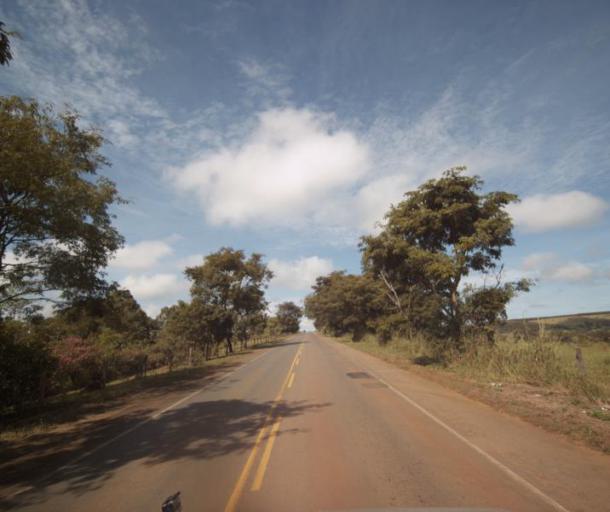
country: BR
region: Goias
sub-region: Pirenopolis
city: Pirenopolis
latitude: -15.9955
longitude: -48.8381
